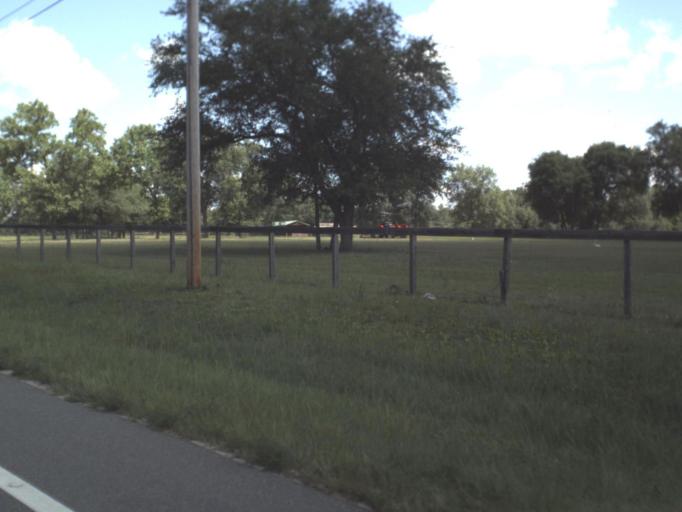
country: US
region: Florida
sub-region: Clay County
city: Keystone Heights
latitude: 29.7428
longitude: -81.9745
